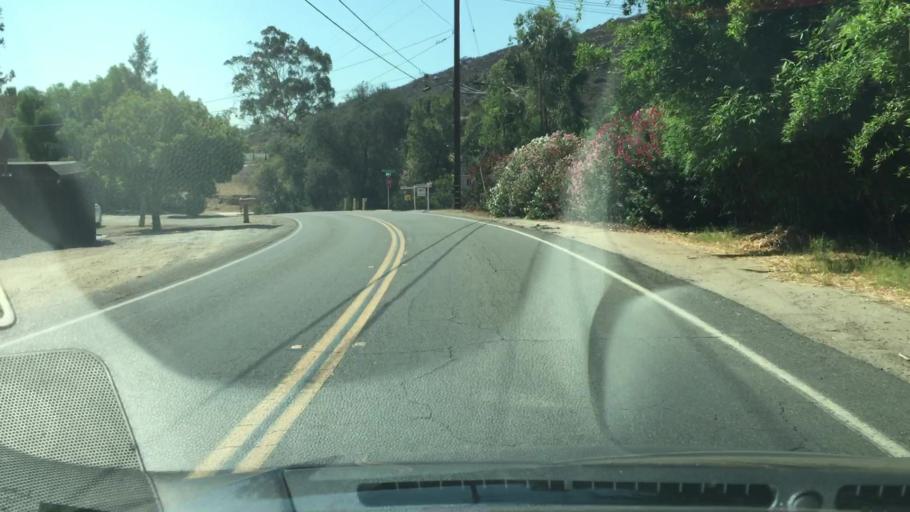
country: US
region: California
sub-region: San Diego County
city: Jamul
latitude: 32.7341
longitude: -116.8835
